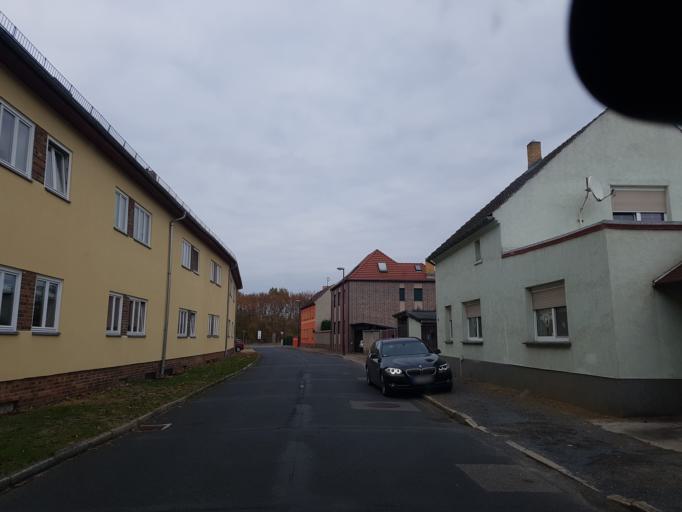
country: DE
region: Brandenburg
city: Finsterwalde
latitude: 51.6250
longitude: 13.6993
